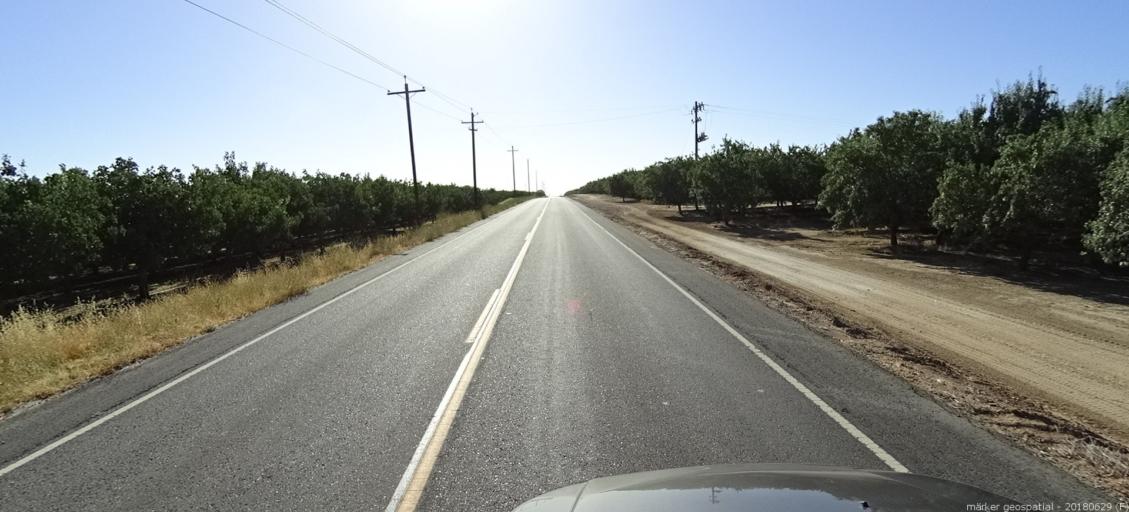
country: US
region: California
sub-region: Madera County
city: Parksdale
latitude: 36.9666
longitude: -119.9617
